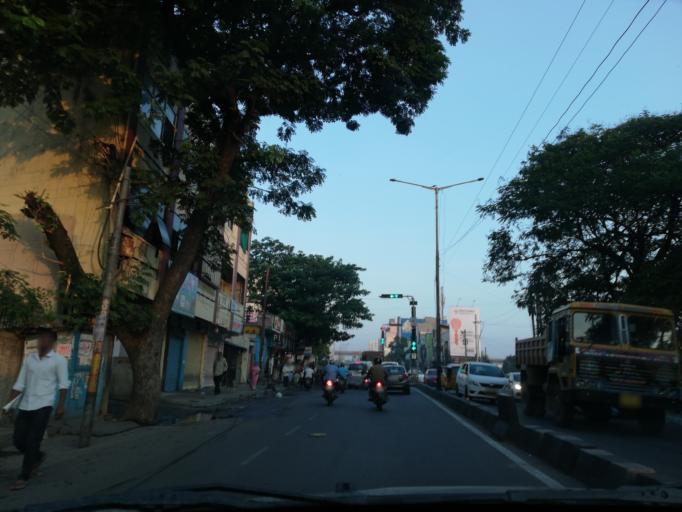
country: IN
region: Telangana
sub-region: Rangareddi
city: Gaddi Annaram
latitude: 17.3960
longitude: 78.4969
